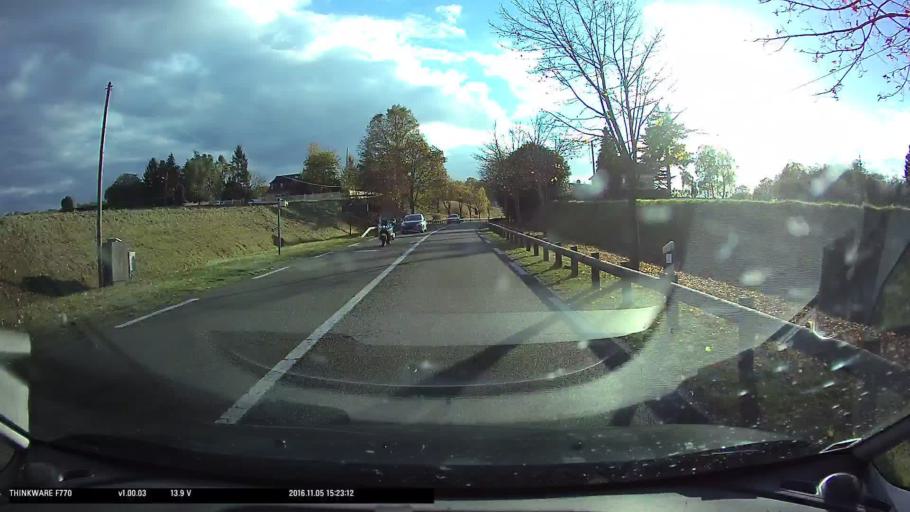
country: FR
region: Ile-de-France
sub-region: Departement du Val-d'Oise
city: Sagy
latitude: 49.0462
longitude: 1.9551
